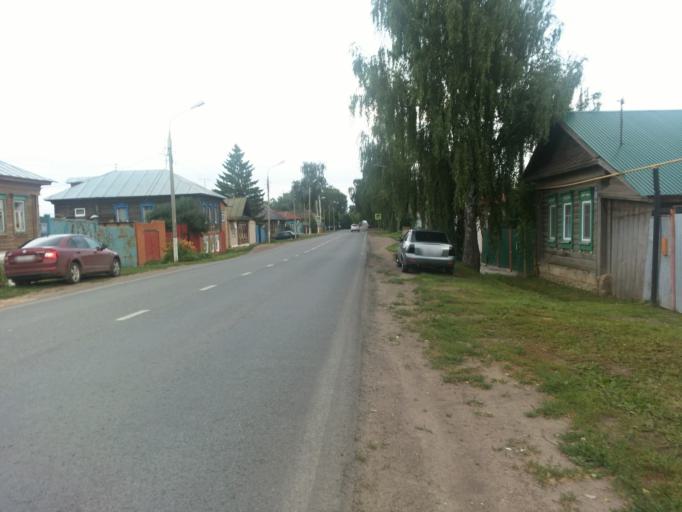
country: RU
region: Tatarstan
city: Yelabuga
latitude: 55.7559
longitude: 52.0741
